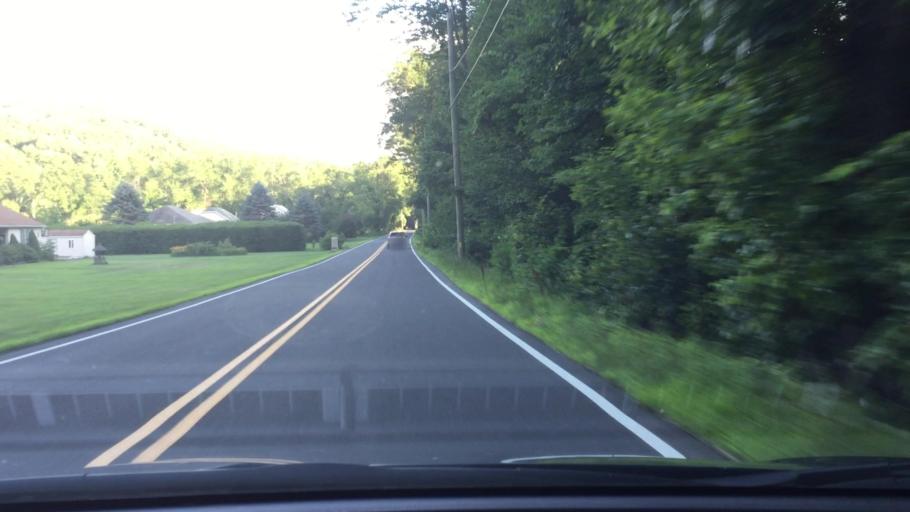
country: US
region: Massachusetts
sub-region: Hampshire County
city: Westhampton
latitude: 42.2252
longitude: -72.8557
